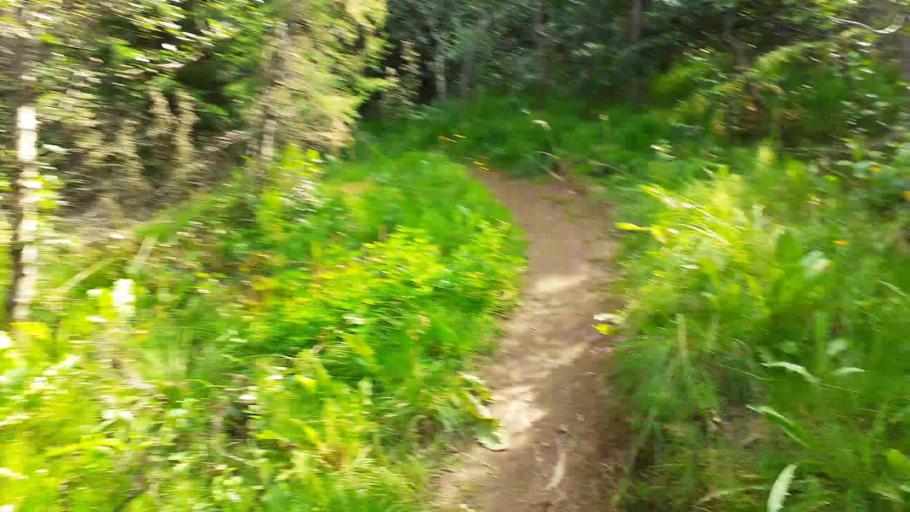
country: IS
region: Northeast
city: Akureyri
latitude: 65.6416
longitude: -18.0847
